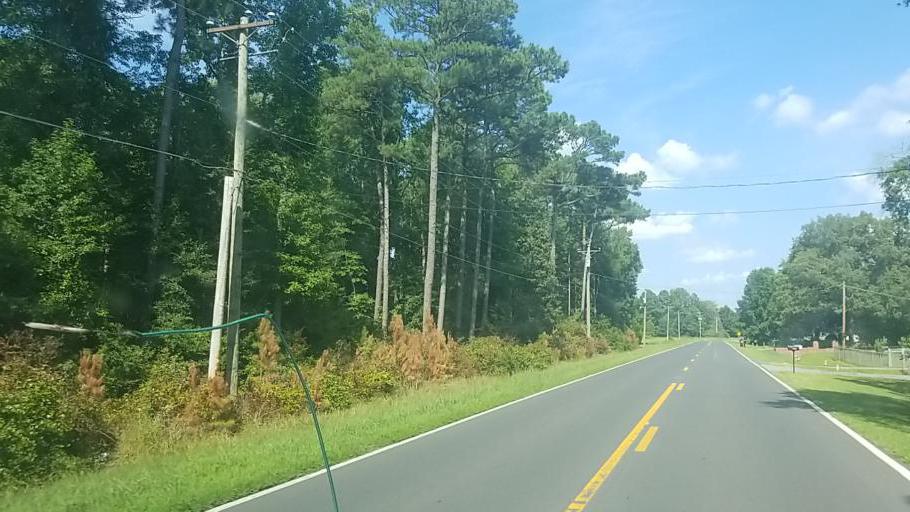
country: US
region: Maryland
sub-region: Wicomico County
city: Fruitland
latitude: 38.3138
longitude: -75.6385
